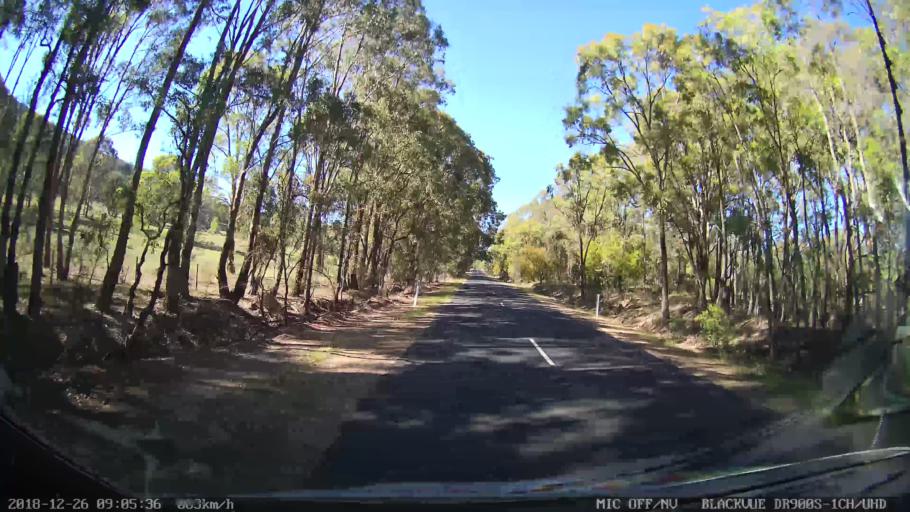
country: AU
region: New South Wales
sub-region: Mid-Western Regional
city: Kandos
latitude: -32.6845
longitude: 150.0065
